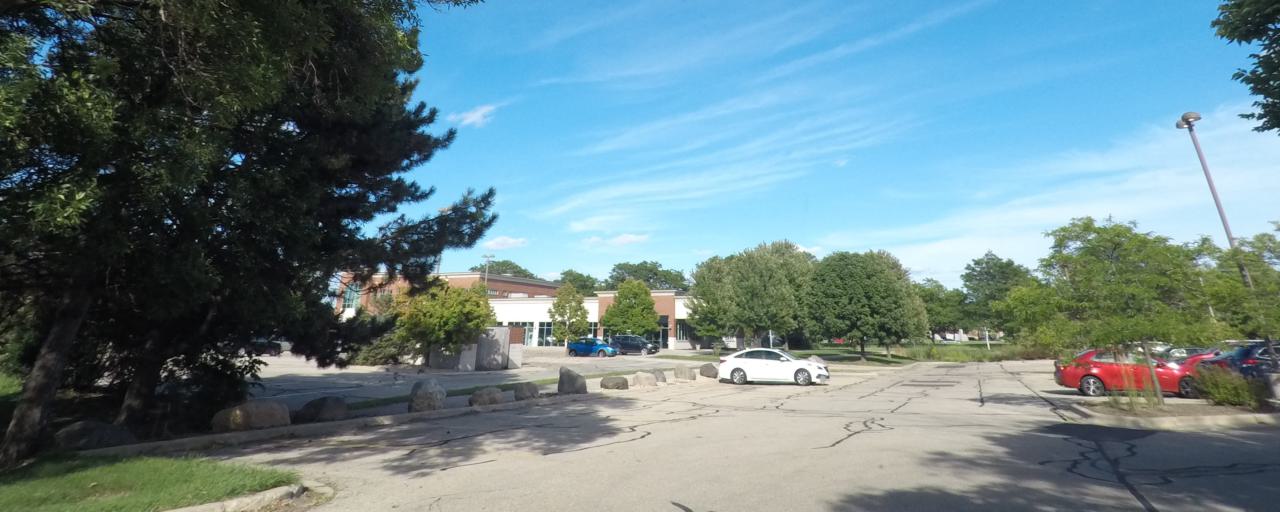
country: US
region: Wisconsin
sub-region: Dane County
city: Middleton
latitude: 43.0648
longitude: -89.5040
